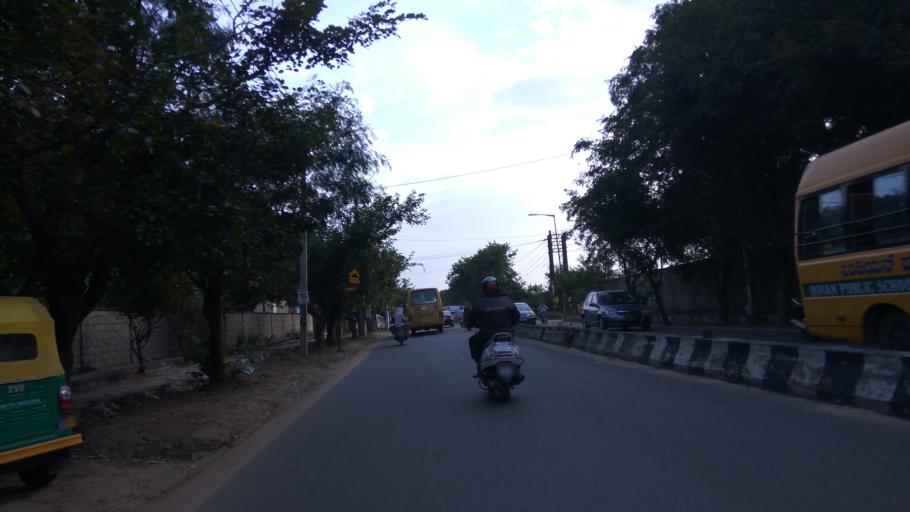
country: IN
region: Karnataka
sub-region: Bangalore Urban
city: Bangalore
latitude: 12.9619
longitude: 77.6906
